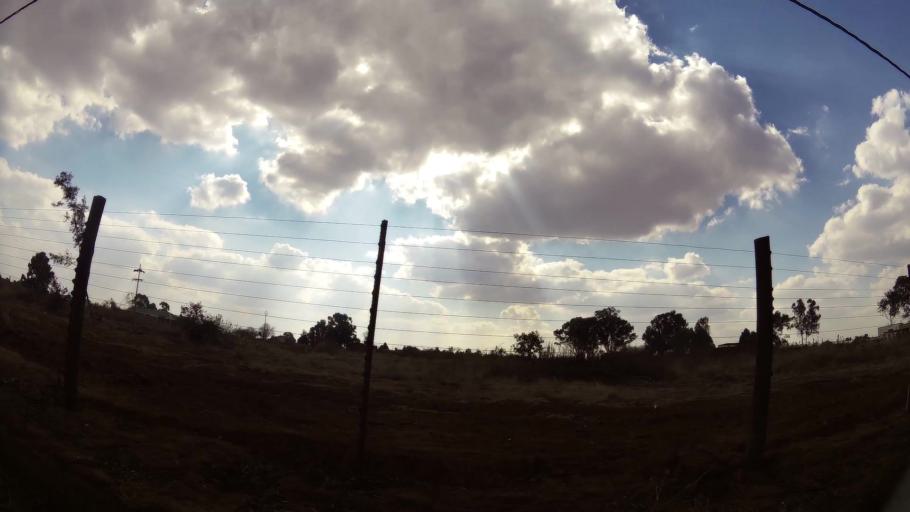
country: ZA
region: Mpumalanga
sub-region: Nkangala District Municipality
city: Delmas
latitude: -26.1319
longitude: 28.6696
